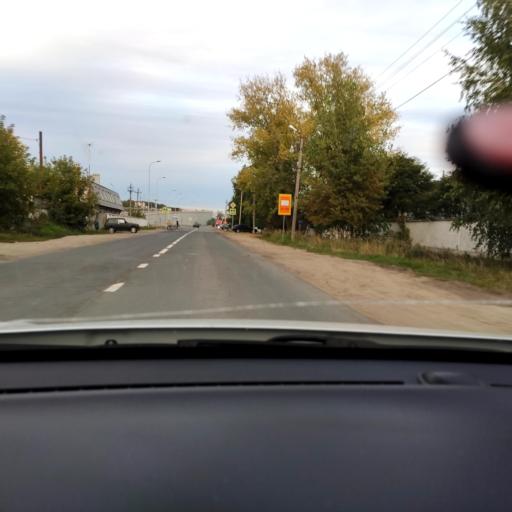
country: RU
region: Tatarstan
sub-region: Zelenodol'skiy Rayon
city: Zelenodolsk
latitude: 55.8393
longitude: 48.5382
